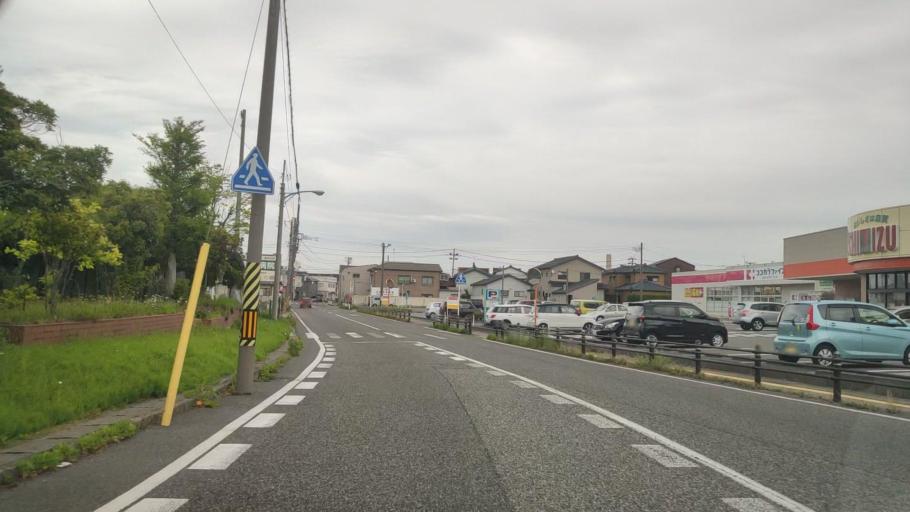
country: JP
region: Niigata
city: Niigata-shi
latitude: 37.9378
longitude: 139.0730
